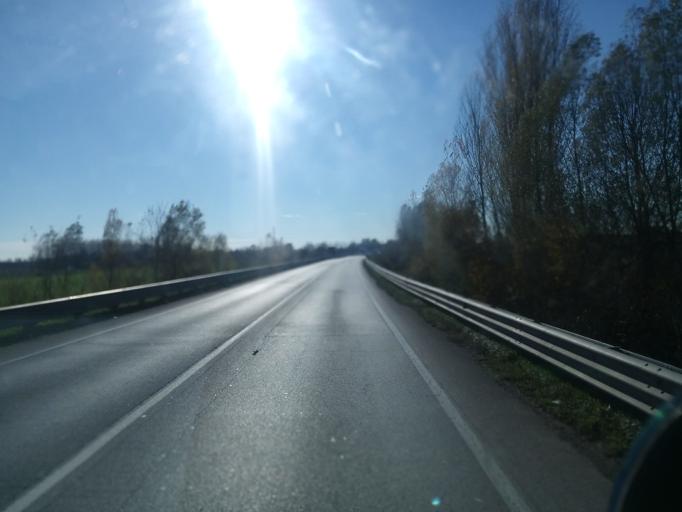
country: IT
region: Veneto
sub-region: Provincia di Padova
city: Loreggia
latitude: 45.5820
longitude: 11.9571
